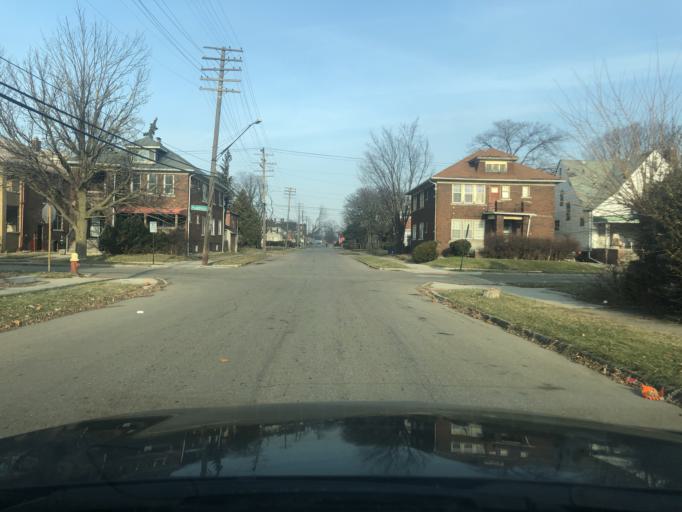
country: US
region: Michigan
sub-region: Wayne County
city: Highland Park
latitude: 42.3931
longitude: -83.1289
